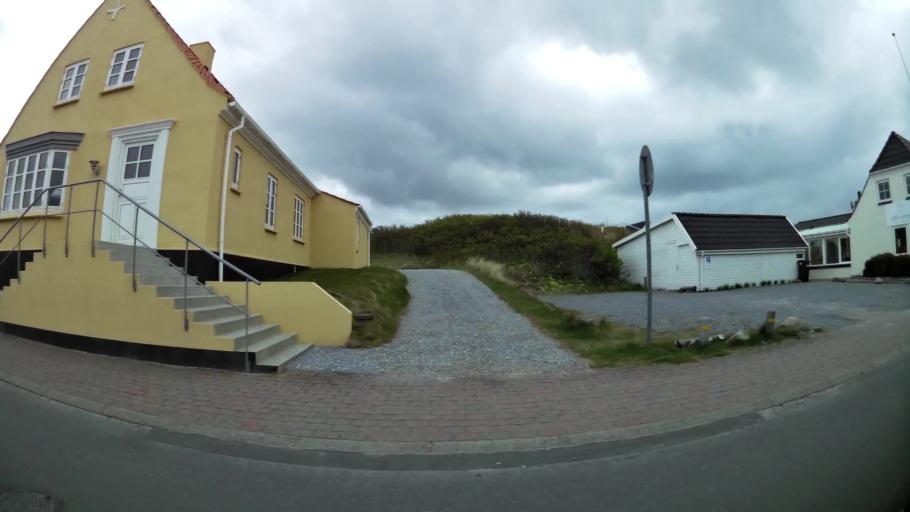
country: DK
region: North Denmark
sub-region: Thisted Kommune
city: Hanstholm
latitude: 57.0417
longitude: 8.4839
